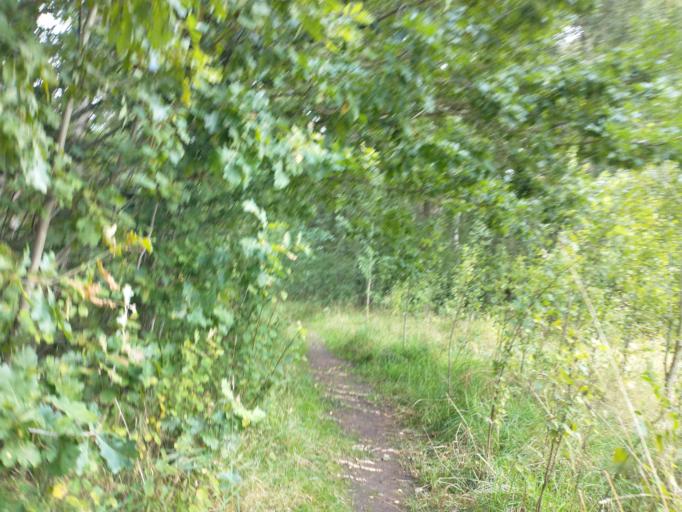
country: SE
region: Kalmar
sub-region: Kalmar Kommun
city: Lindsdal
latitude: 56.7781
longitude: 16.2969
